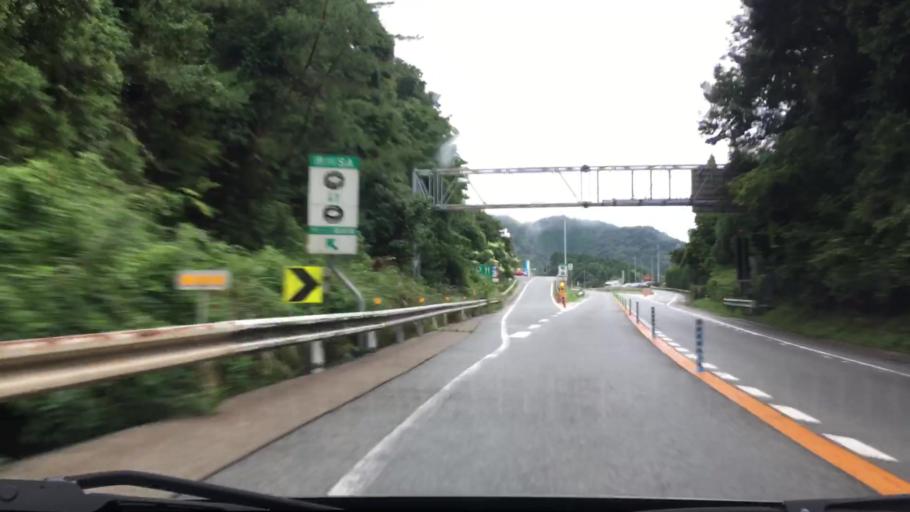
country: JP
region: Hyogo
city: Nishiwaki
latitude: 35.0272
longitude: 134.7669
